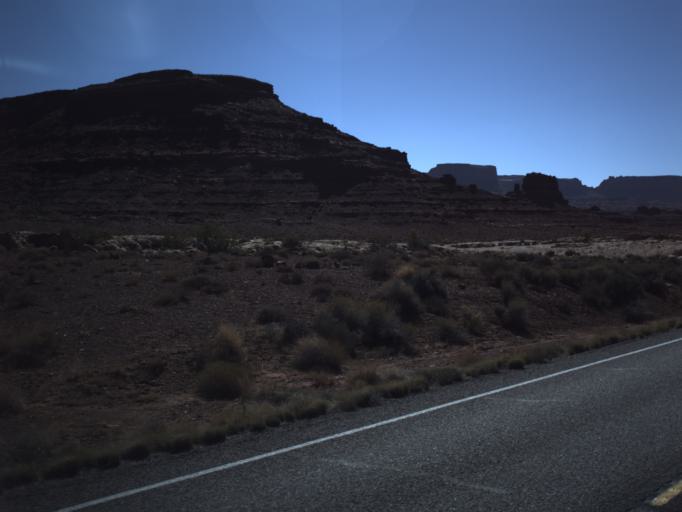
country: US
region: Utah
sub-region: San Juan County
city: Blanding
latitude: 37.8437
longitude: -110.3554
